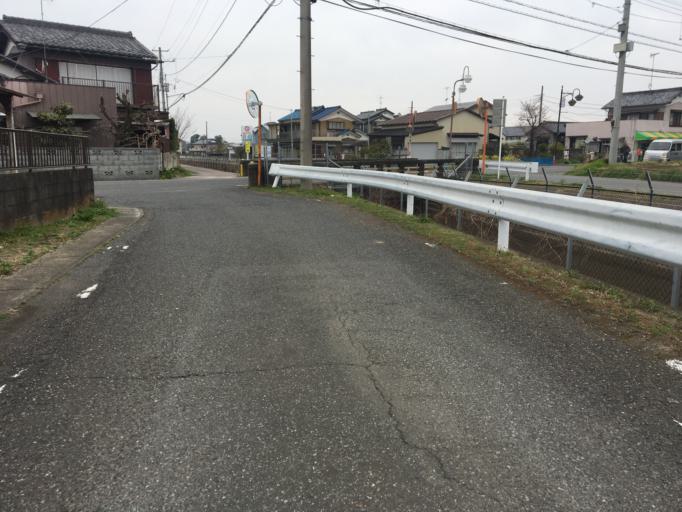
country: JP
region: Saitama
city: Kazo
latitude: 36.1112
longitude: 139.5917
